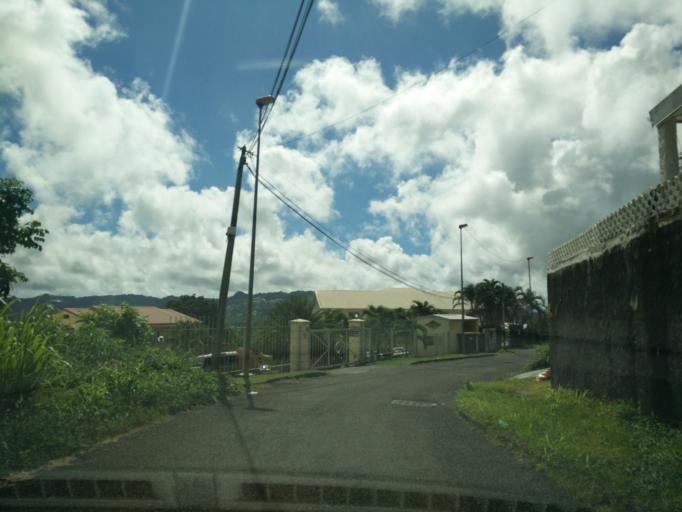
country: MQ
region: Martinique
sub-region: Martinique
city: Le Lamentin
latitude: 14.6258
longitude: -61.0145
